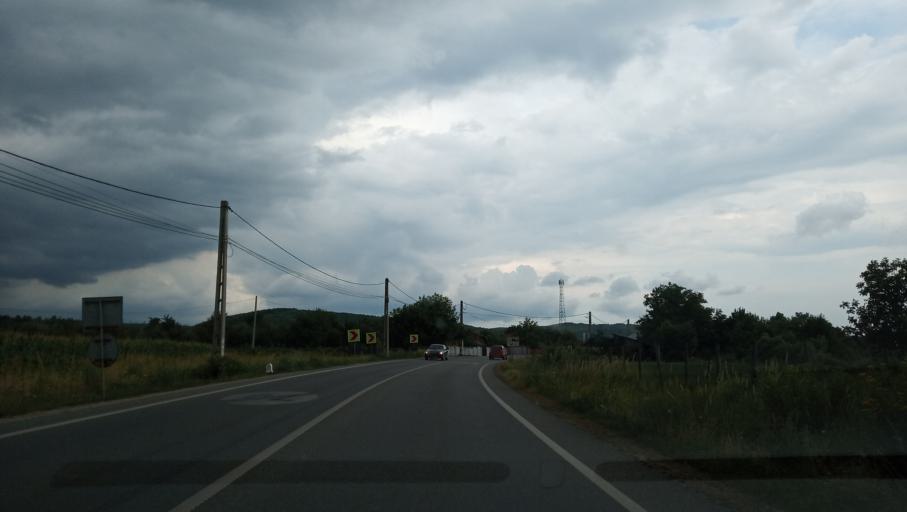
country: RO
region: Gorj
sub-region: Oras Rovinari
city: Rovinari
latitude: 44.9018
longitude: 23.2020
